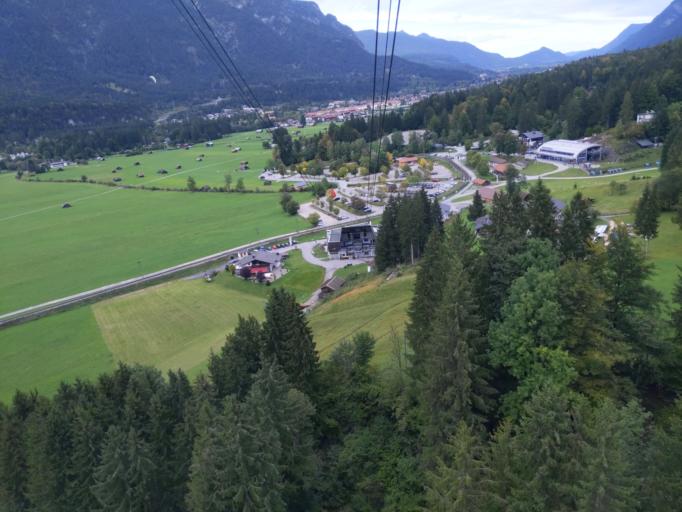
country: DE
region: Bavaria
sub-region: Upper Bavaria
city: Grainau
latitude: 47.4685
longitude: 11.0606
